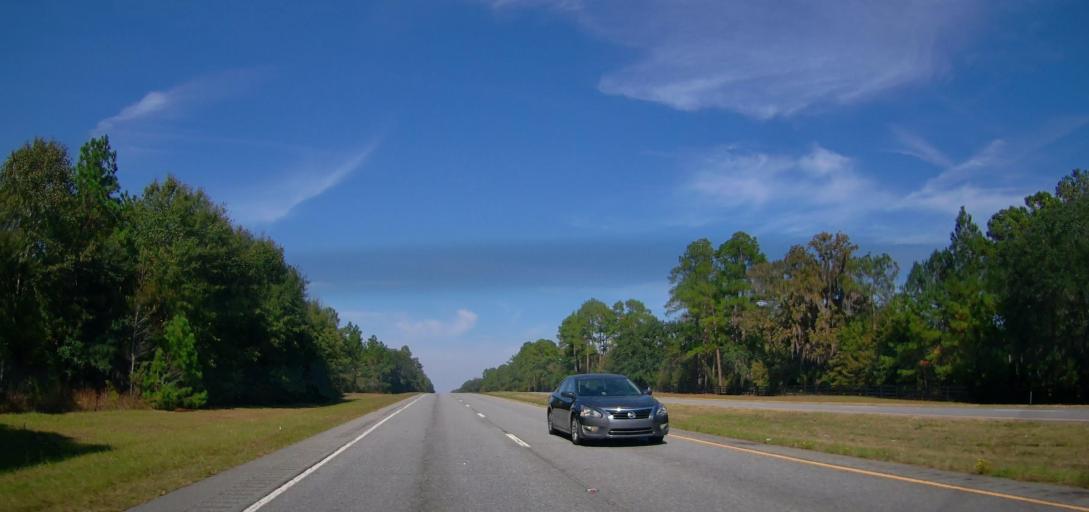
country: US
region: Georgia
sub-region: Lee County
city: Leesburg
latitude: 31.6863
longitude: -83.9938
